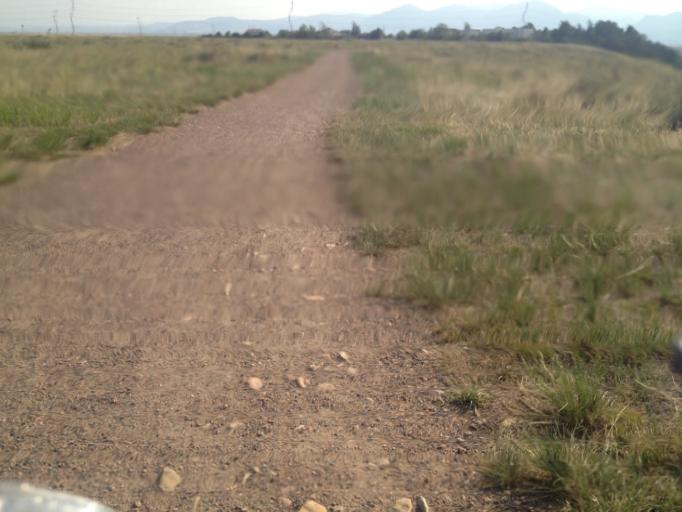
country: US
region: Colorado
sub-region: Boulder County
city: Superior
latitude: 39.9772
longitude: -105.1719
